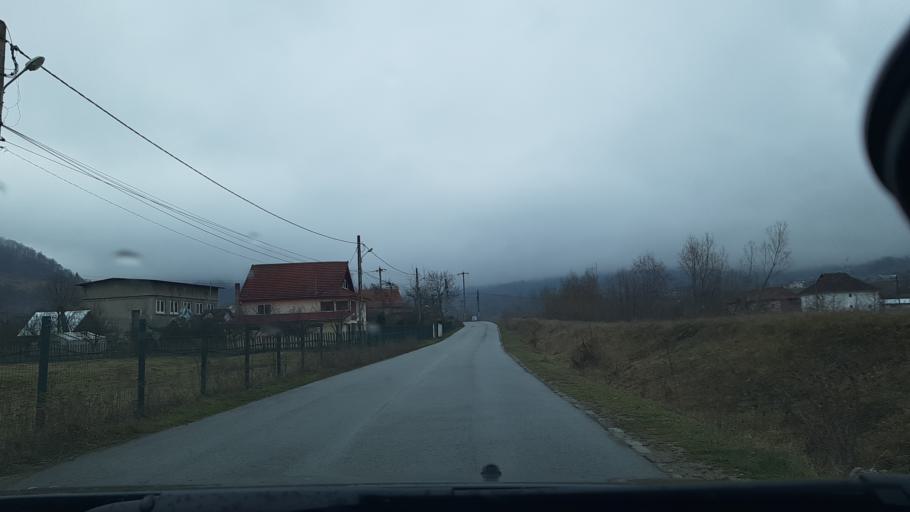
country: RO
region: Hunedoara
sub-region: Oras Petrila
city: Petrila
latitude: 45.4268
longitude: 23.4231
